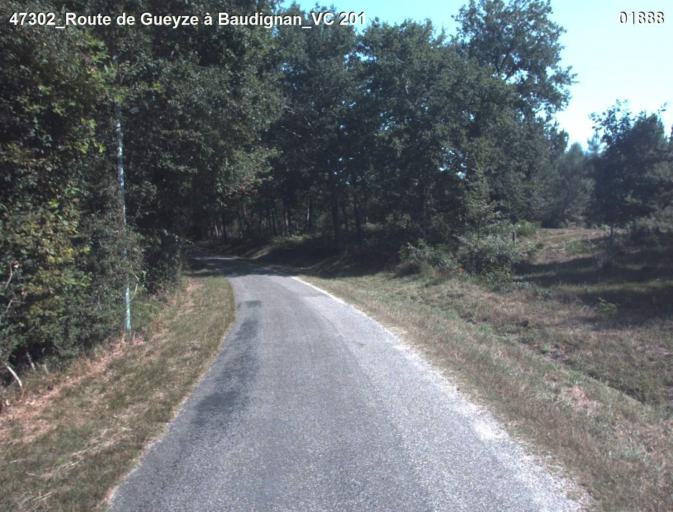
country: FR
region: Aquitaine
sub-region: Departement des Landes
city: Gabarret
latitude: 44.0551
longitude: 0.1152
